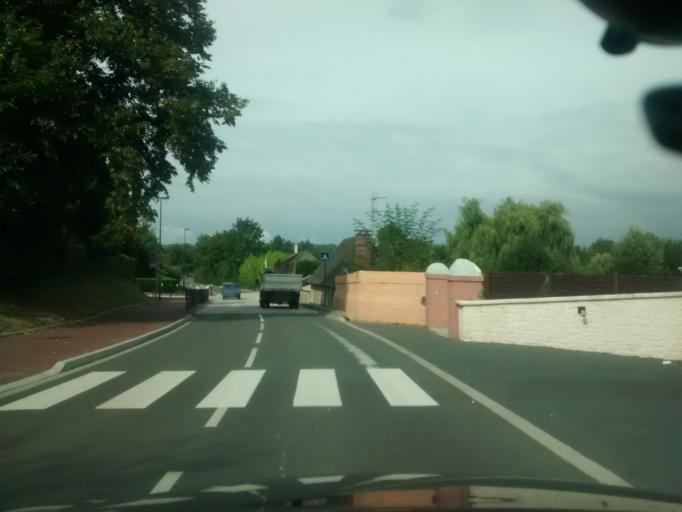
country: FR
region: Lower Normandy
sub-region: Departement du Calvados
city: Touques
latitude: 49.3326
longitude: 0.0897
